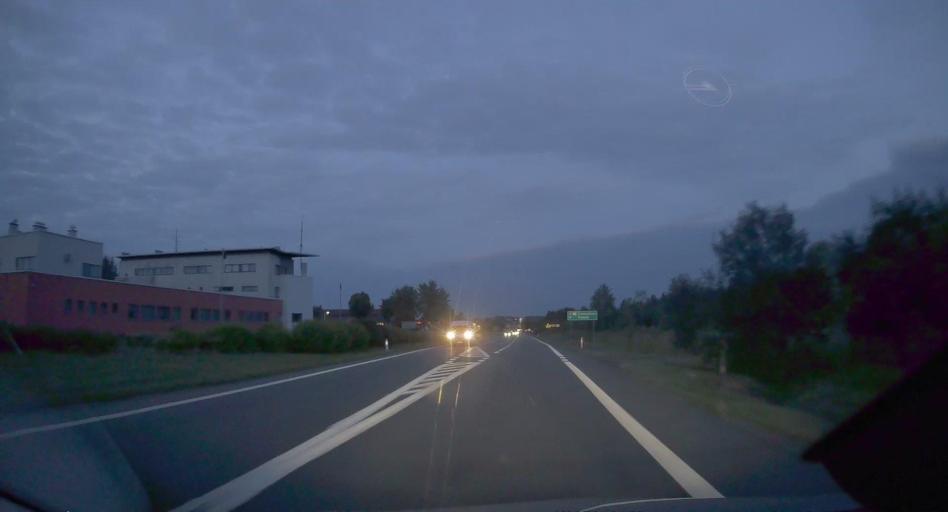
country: PL
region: Silesian Voivodeship
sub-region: Powiat klobucki
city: Klobuck
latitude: 50.9076
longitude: 18.9163
